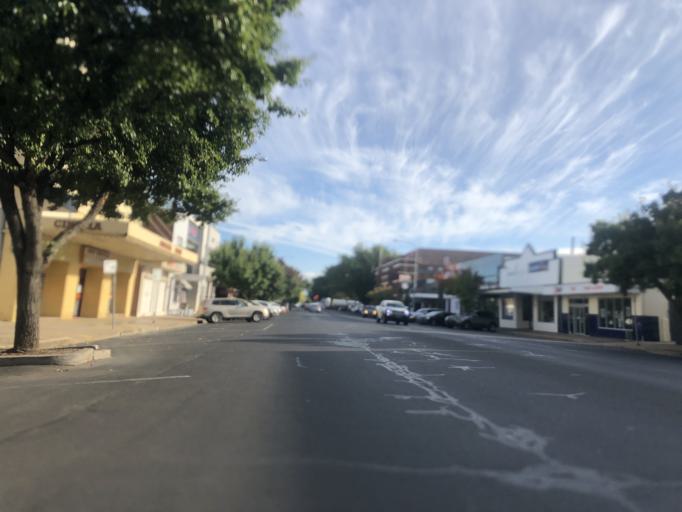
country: AU
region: New South Wales
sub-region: Orange Municipality
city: Orange
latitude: -33.2853
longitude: 149.1008
